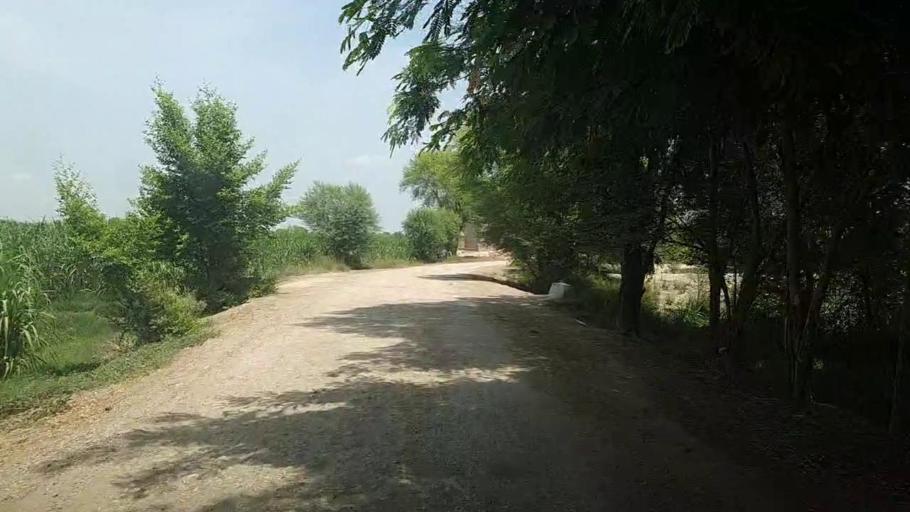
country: PK
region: Sindh
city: Ubauro
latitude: 28.2423
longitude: 69.8248
